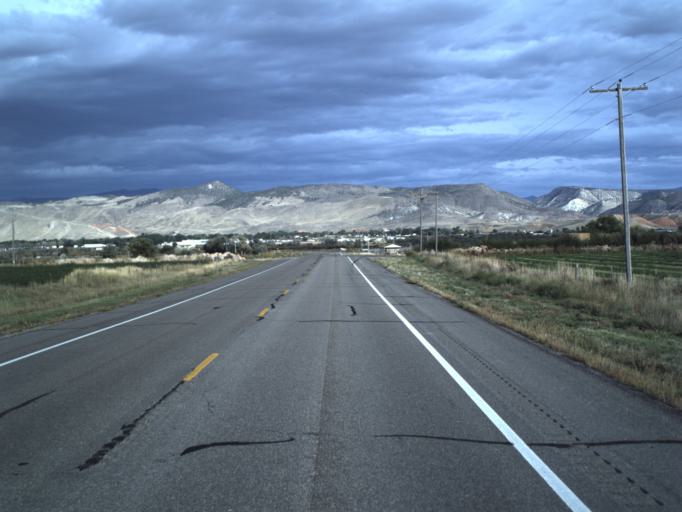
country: US
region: Utah
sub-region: Sevier County
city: Salina
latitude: 38.9542
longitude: -111.9013
